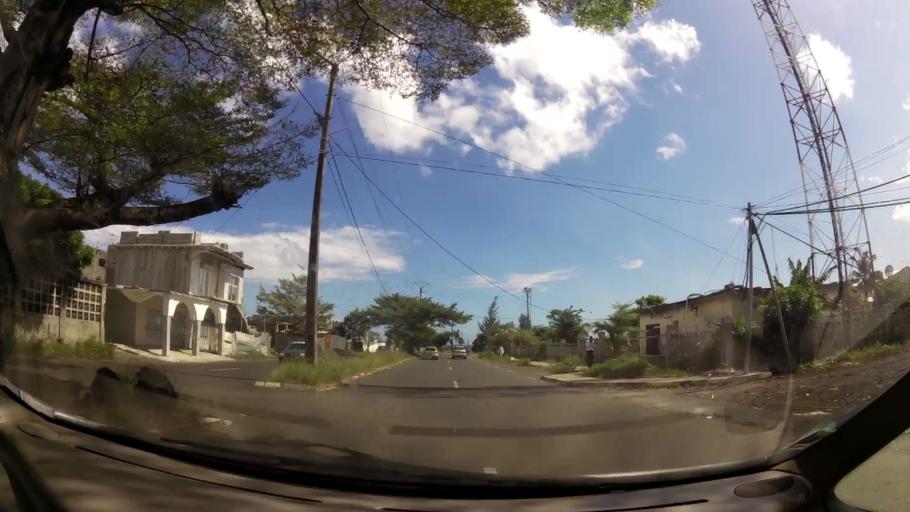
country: KM
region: Grande Comore
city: Mavingouni
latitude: -11.7194
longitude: 43.2467
